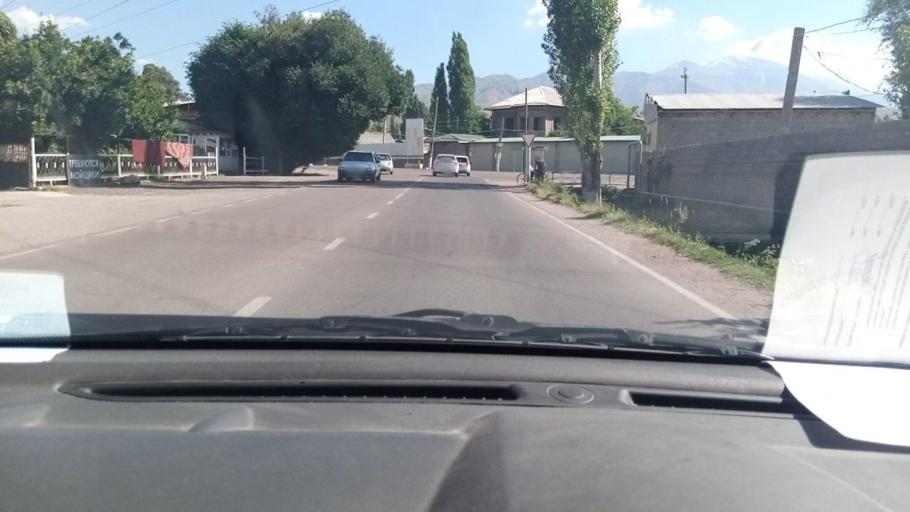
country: UZ
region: Toshkent
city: Angren
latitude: 41.0381
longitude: 70.0941
